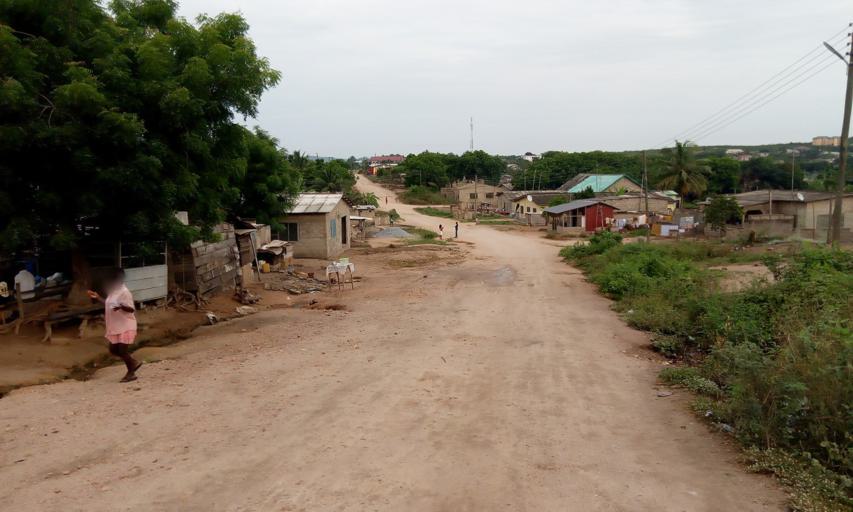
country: GH
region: Central
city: Winneba
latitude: 5.3557
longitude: -0.6164
